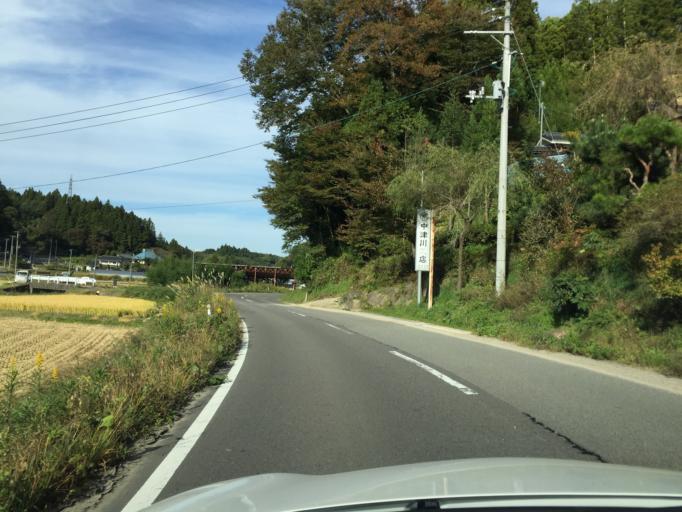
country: JP
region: Fukushima
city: Miharu
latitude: 37.3481
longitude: 140.5097
